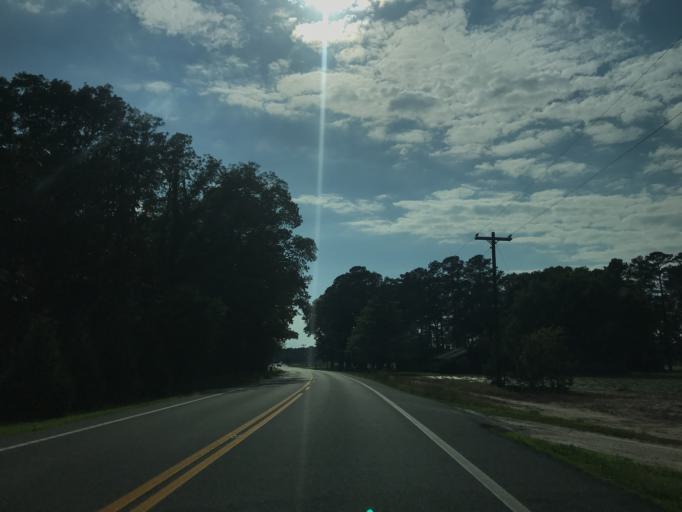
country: US
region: Maryland
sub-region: Wicomico County
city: Hebron
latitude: 38.4658
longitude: -75.7129
